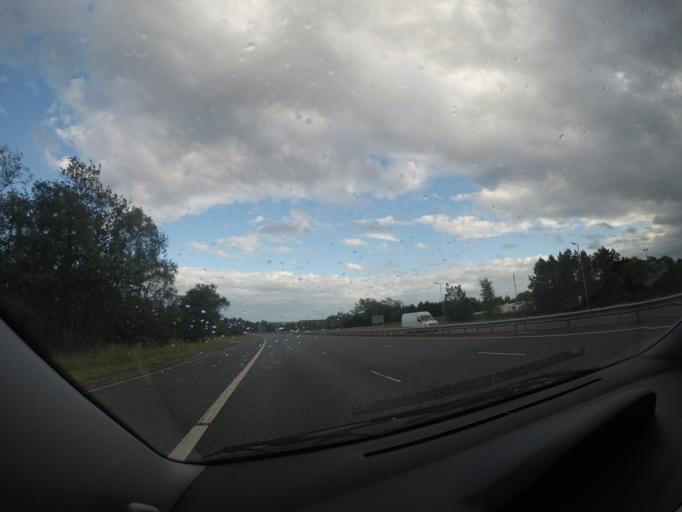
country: GB
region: Scotland
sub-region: Dumfries and Galloway
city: Gretna
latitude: 54.9991
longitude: -3.0575
